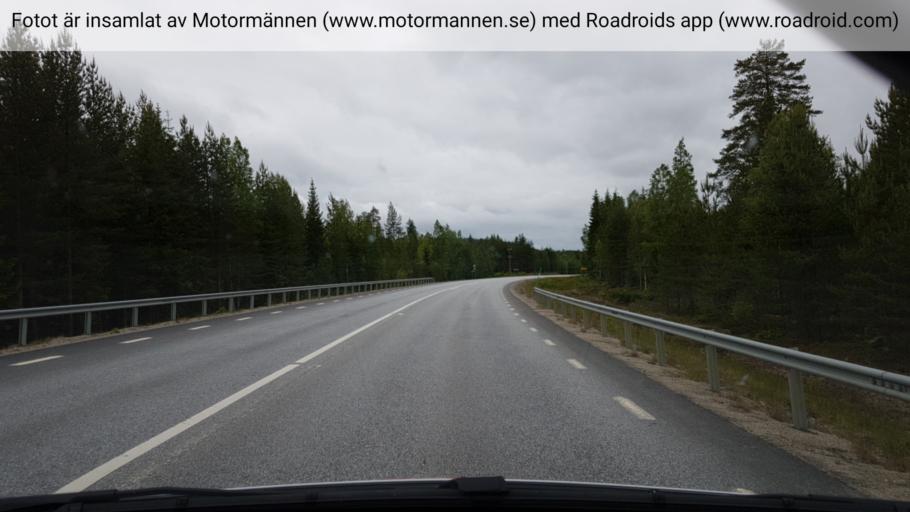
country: SE
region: Vaesterbotten
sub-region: Vannas Kommun
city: Vaennaes
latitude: 64.0133
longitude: 19.6941
